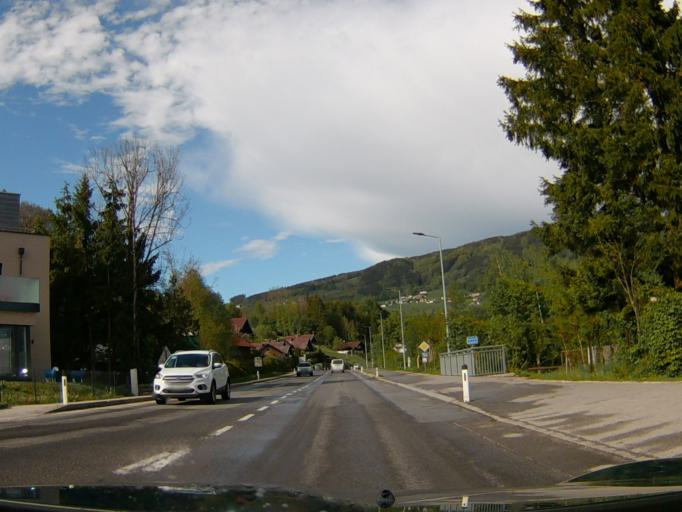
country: AT
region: Upper Austria
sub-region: Politischer Bezirk Vocklabruck
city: Mondsee
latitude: 47.8477
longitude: 13.3402
